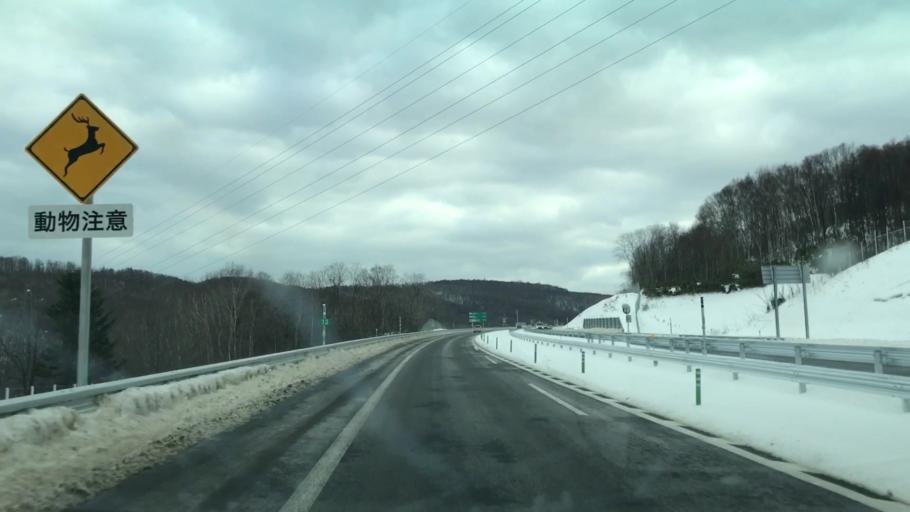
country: JP
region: Hokkaido
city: Otaru
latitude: 43.1991
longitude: 140.9450
